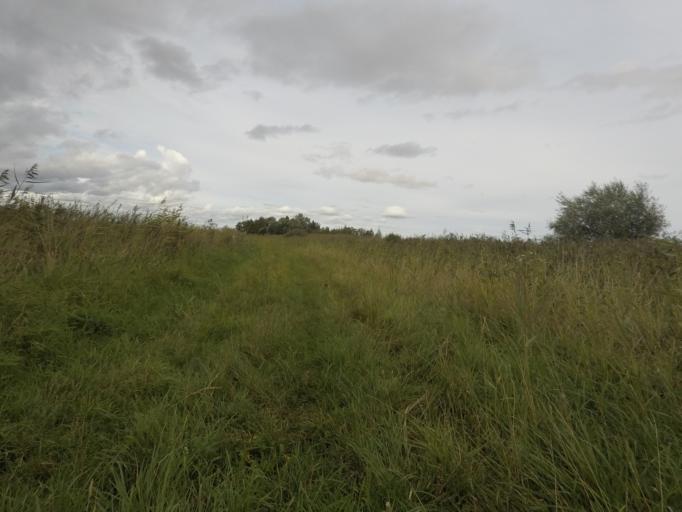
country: SE
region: Vaestmanland
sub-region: Kungsors Kommun
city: Kungsoer
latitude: 59.4603
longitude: 16.0612
